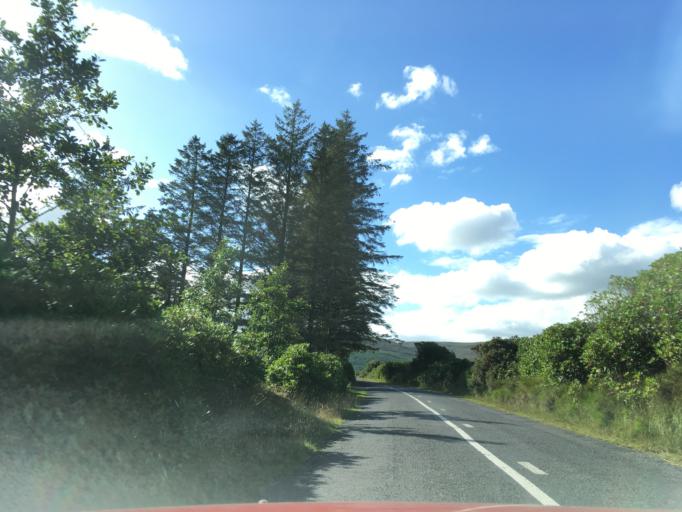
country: IE
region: Munster
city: Cahir
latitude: 52.2143
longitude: -7.9344
